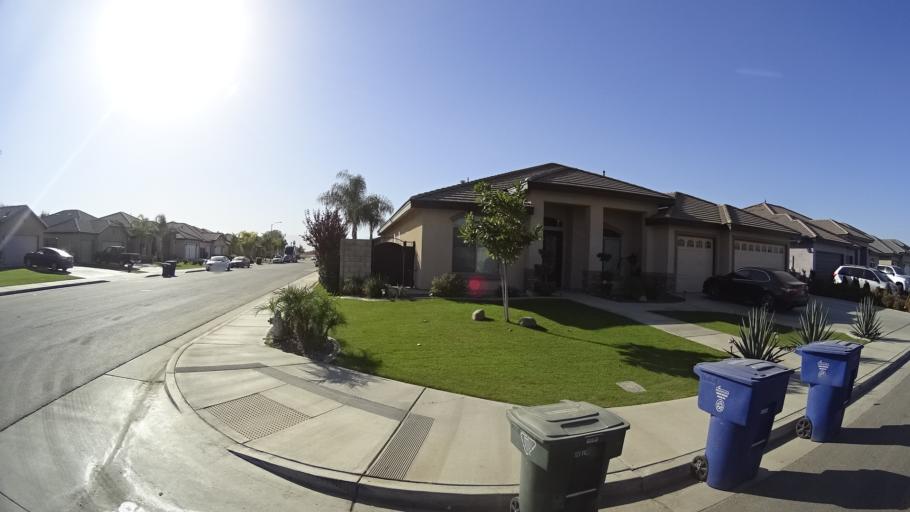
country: US
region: California
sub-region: Kern County
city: Greenfield
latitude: 35.2727
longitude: -119.0463
